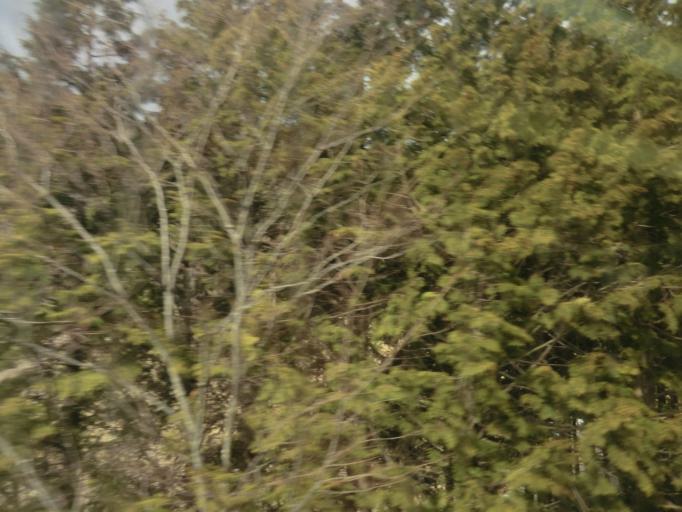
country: JP
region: Nagano
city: Ina
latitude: 35.8797
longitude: 137.7540
